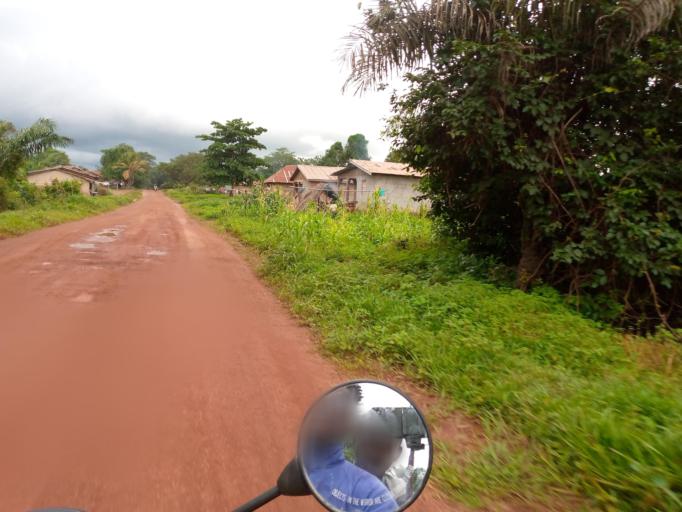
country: SL
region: Northern Province
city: Port Loko
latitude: 8.8833
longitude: -12.7237
